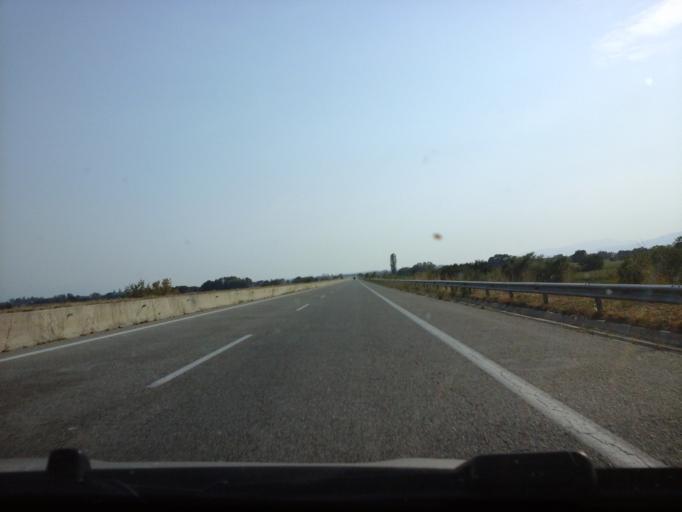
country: GR
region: East Macedonia and Thrace
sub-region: Nomos Xanthis
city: Selero
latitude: 41.1139
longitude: 24.9782
